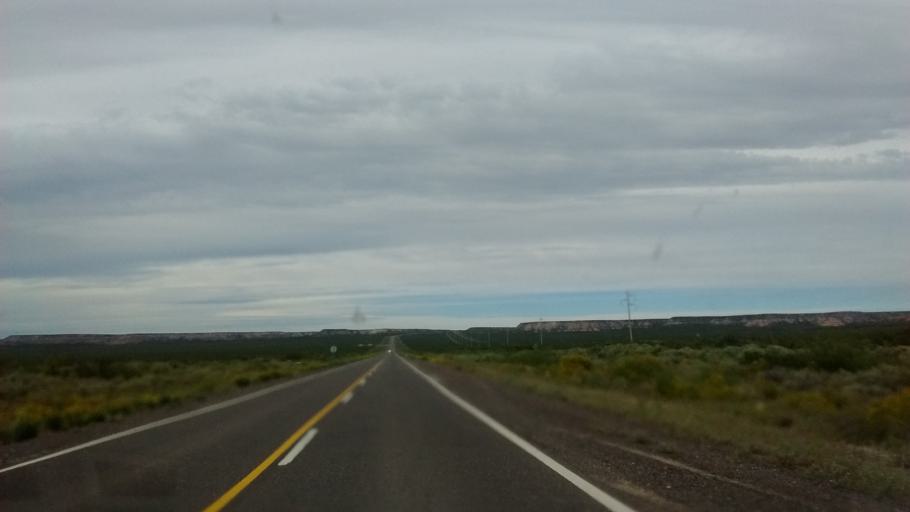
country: AR
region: Rio Negro
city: Catriel
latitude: -38.1595
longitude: -67.9474
